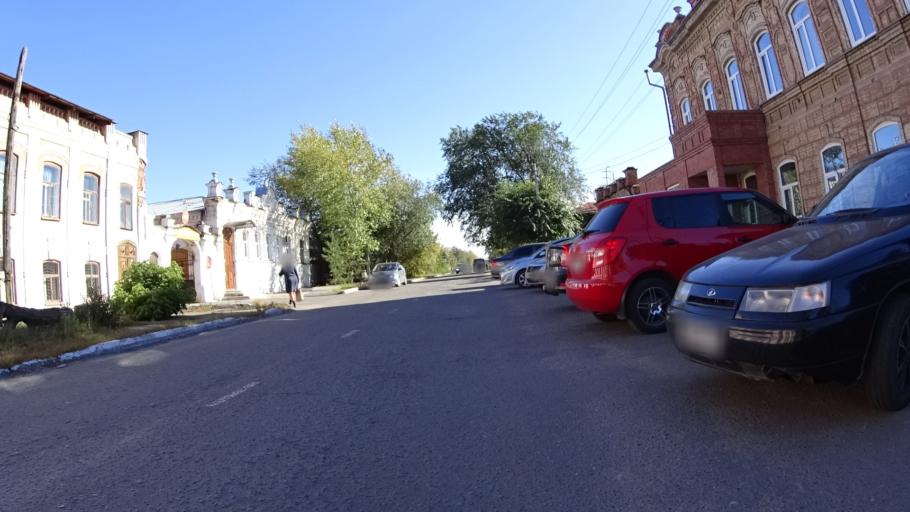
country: RU
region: Chelyabinsk
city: Troitsk
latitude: 54.0831
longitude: 61.5553
